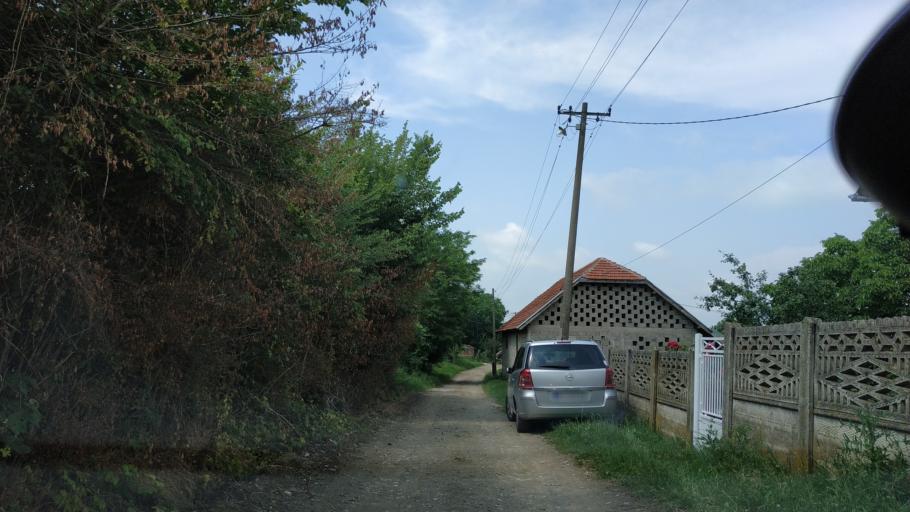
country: RS
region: Central Serbia
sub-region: Nisavski Okrug
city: Aleksinac
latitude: 43.4139
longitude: 21.7170
